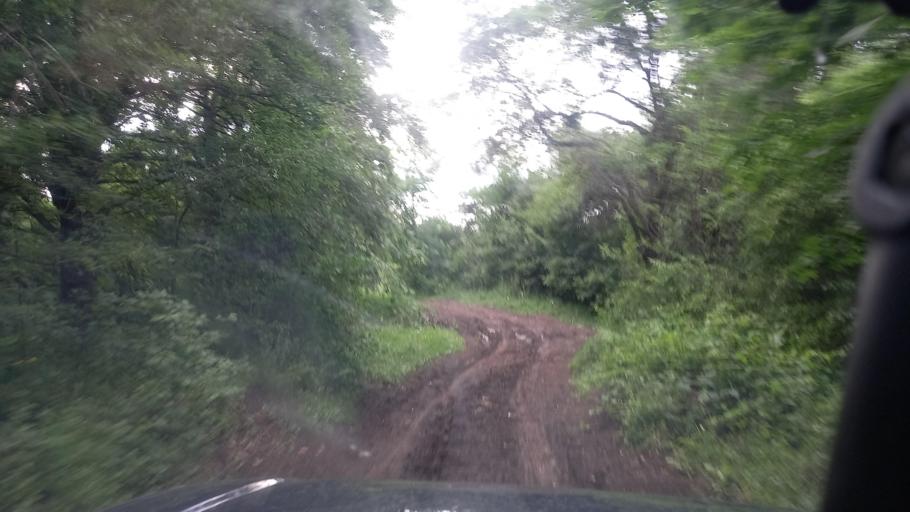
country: RU
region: Karachayevo-Cherkesiya
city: Kurdzhinovo
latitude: 44.1259
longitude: 41.0793
